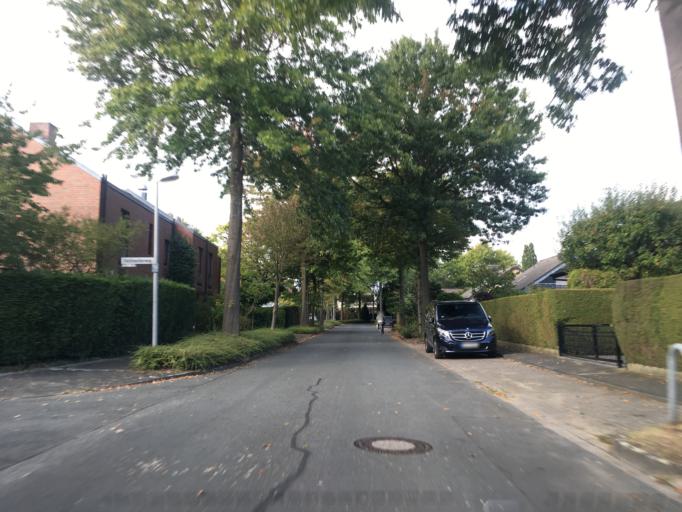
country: DE
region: North Rhine-Westphalia
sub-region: Regierungsbezirk Munster
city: Muenster
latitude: 51.9521
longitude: 7.5247
